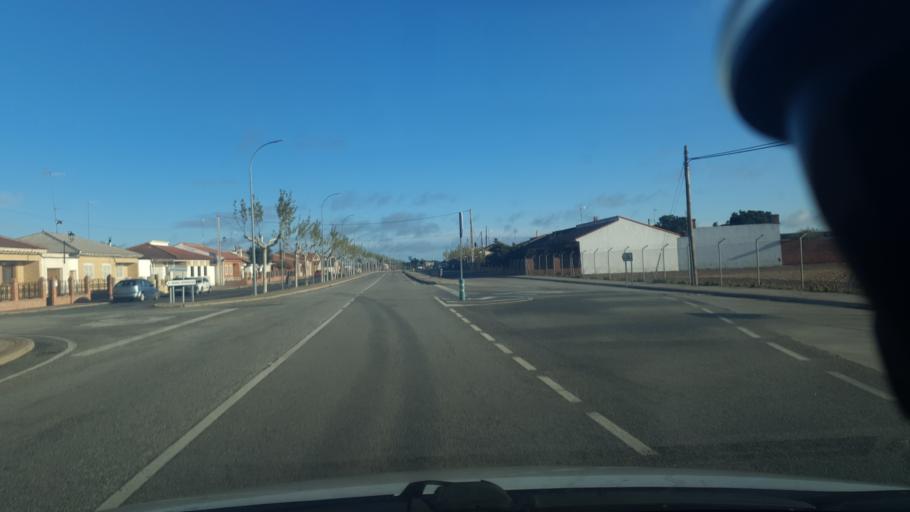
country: ES
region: Castille and Leon
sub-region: Provincia de Avila
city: Tinosillos
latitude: 40.9369
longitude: -4.7263
